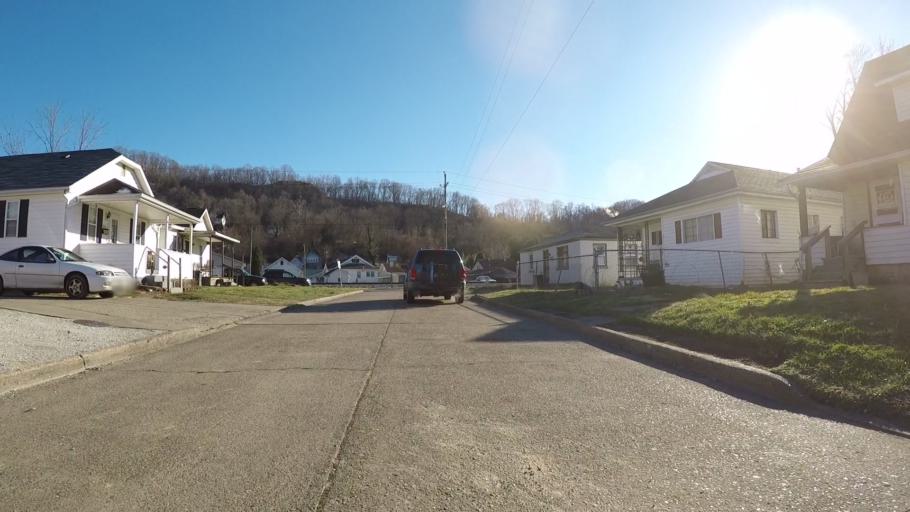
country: US
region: West Virginia
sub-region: Cabell County
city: Pea Ridge
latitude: 38.4296
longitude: -82.3766
